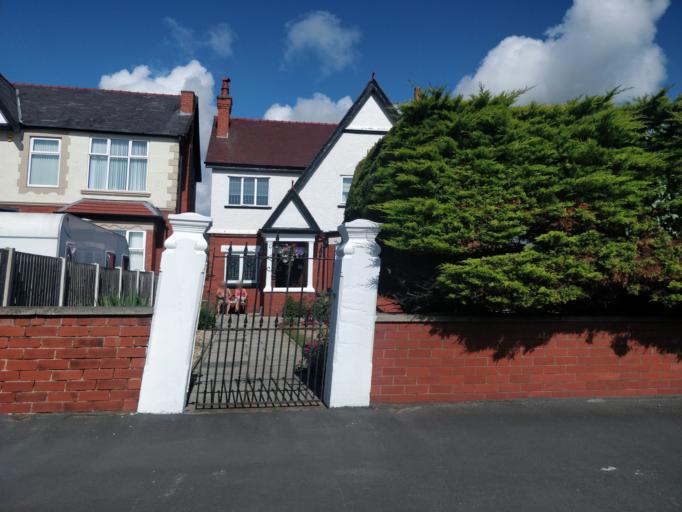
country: GB
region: England
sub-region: Sefton
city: Southport
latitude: 53.6487
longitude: -2.9768
